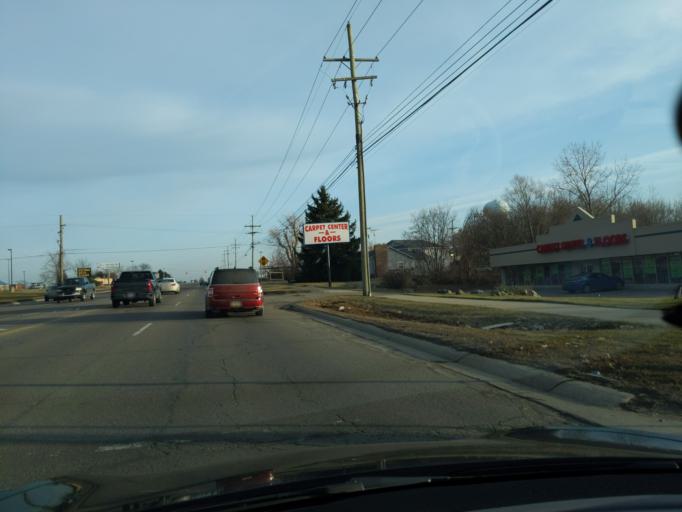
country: US
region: Michigan
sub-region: Livingston County
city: Howell
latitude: 42.5907
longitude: -83.8850
